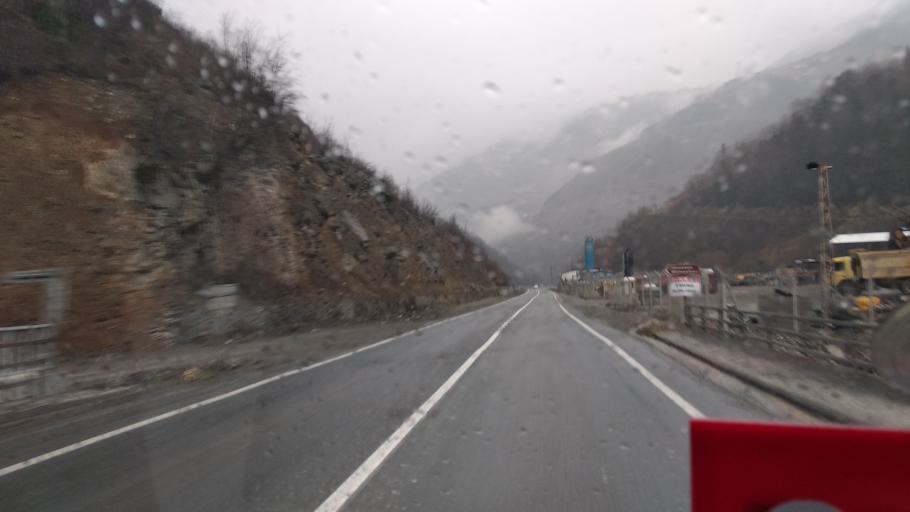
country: TR
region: Trabzon
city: Macka
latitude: 40.7415
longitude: 39.5520
